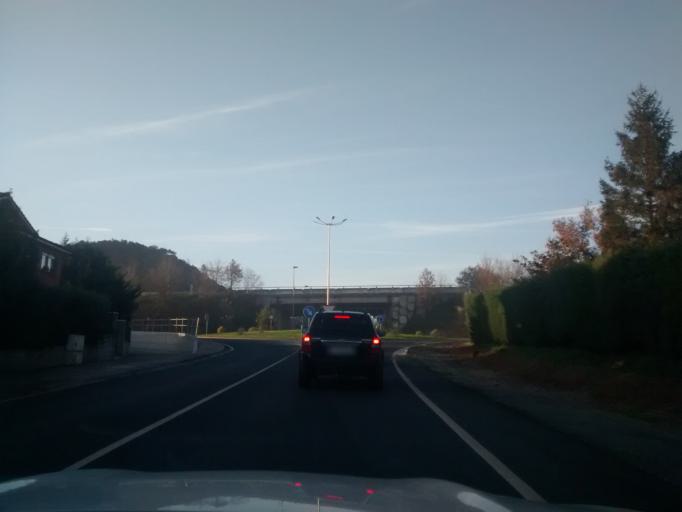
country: ES
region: Cantabria
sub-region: Provincia de Cantabria
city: Lierganes
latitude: 43.3855
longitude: -3.7421
